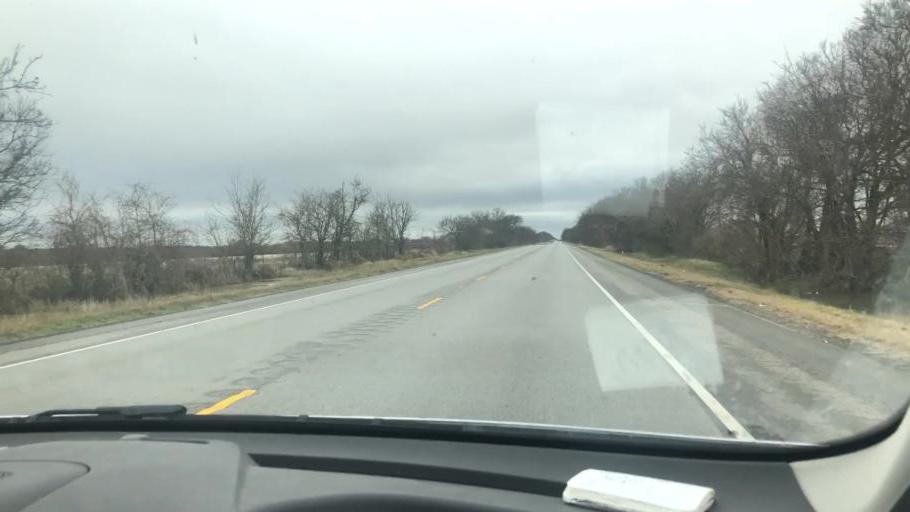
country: US
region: Texas
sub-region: Matagorda County
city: Van Vleck
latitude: 29.1182
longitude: -95.9805
